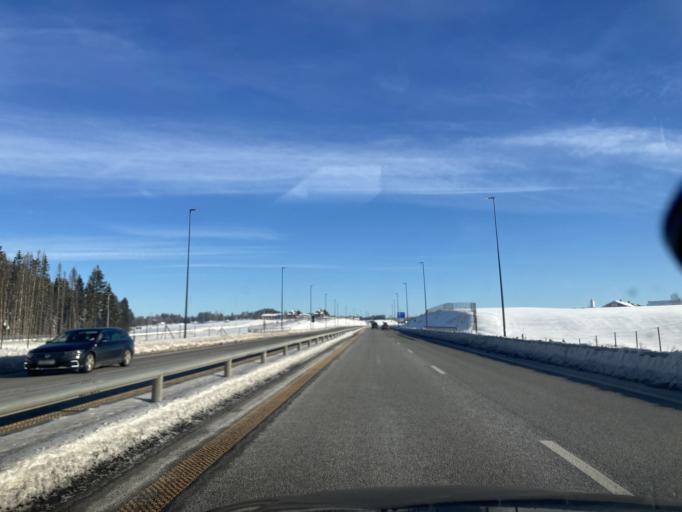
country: NO
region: Hedmark
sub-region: Loten
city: Loten
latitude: 60.8451
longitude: 11.3585
